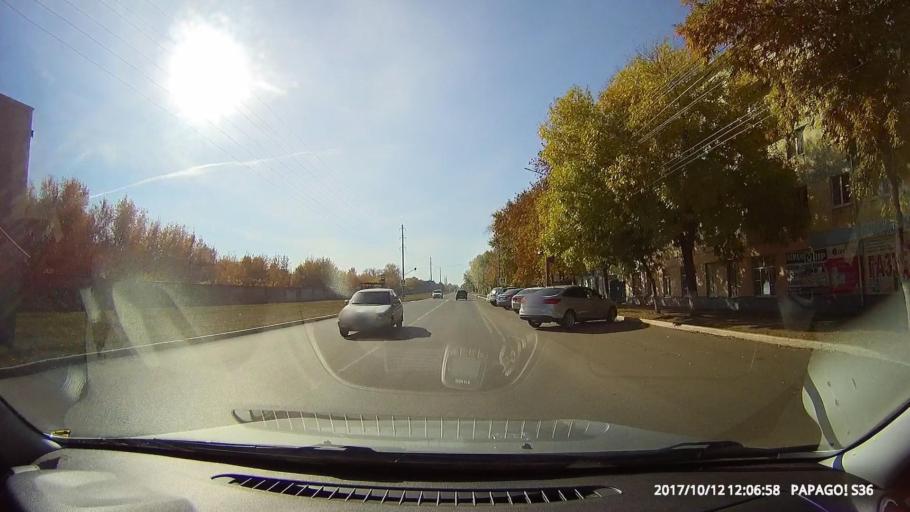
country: RU
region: Samara
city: Chapayevsk
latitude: 52.9698
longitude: 49.7042
